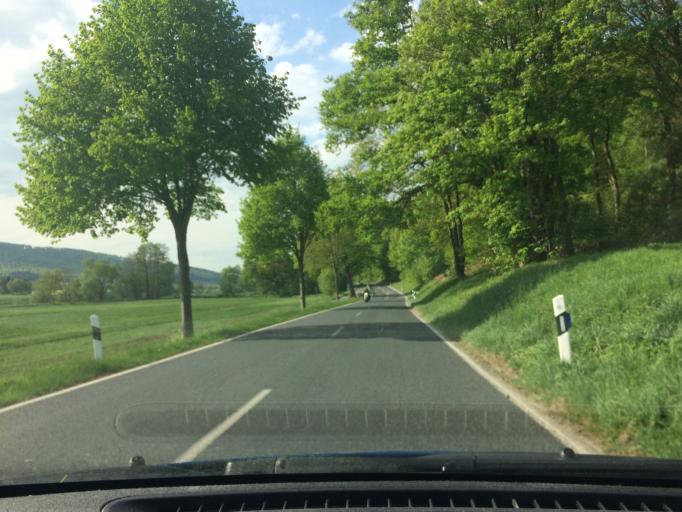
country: DE
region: Lower Saxony
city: Buhren
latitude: 51.5550
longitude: 9.6129
